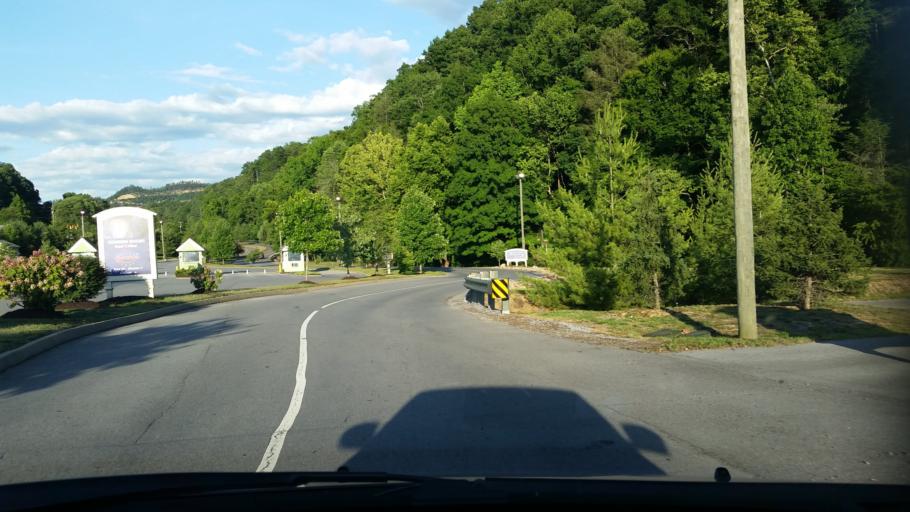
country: US
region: Tennessee
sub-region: Sevier County
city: Pigeon Forge
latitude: 35.8054
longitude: -83.5318
